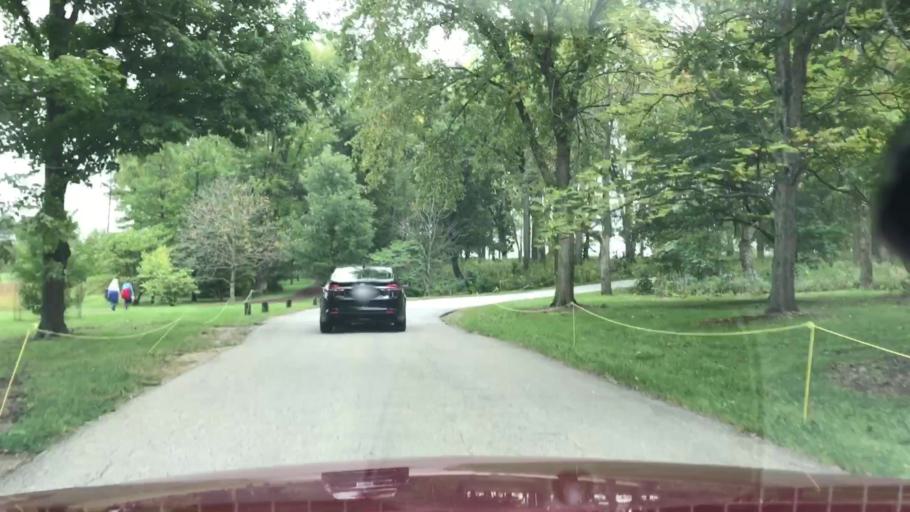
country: US
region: Illinois
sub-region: DuPage County
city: Lisle
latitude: 41.8142
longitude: -88.0655
